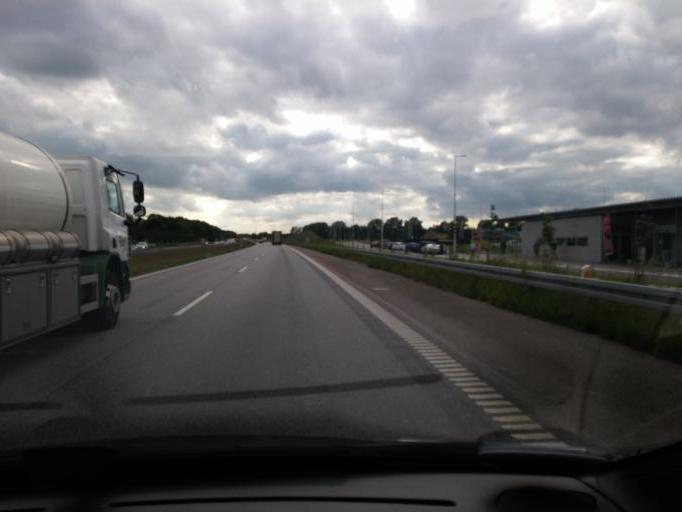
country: DK
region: Zealand
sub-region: Koge Kommune
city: Borup
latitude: 55.4583
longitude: 11.9362
